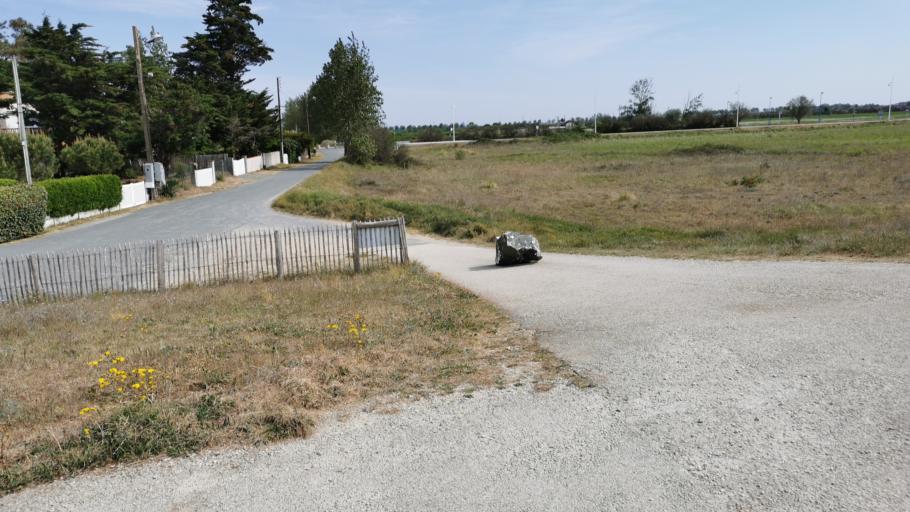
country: FR
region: Pays de la Loire
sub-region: Departement de la Vendee
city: Angles
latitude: 46.3419
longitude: -1.3444
